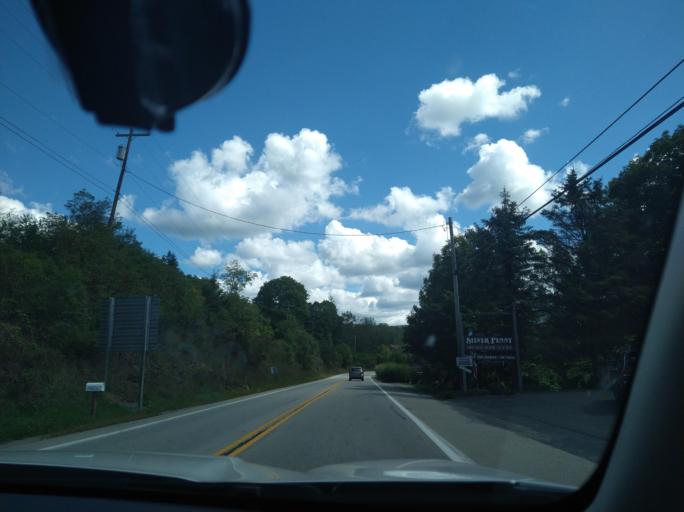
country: US
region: Pennsylvania
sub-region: Fayette County
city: Bear Rocks
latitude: 40.0909
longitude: -79.3464
